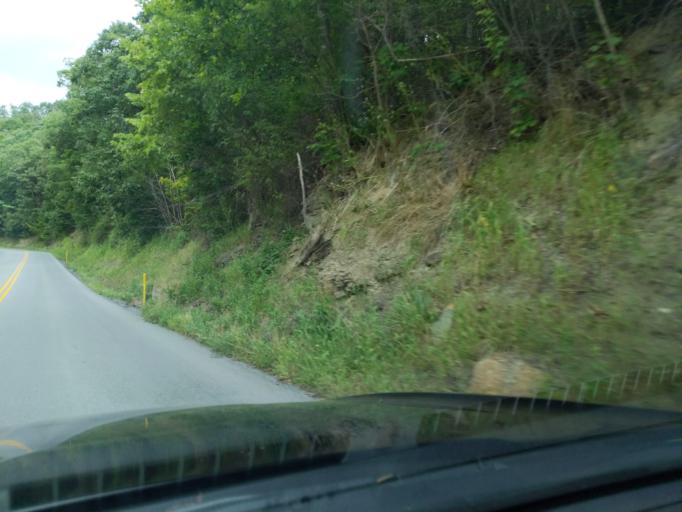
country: US
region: Pennsylvania
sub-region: Blair County
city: Claysburg
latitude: 40.3563
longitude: -78.4690
